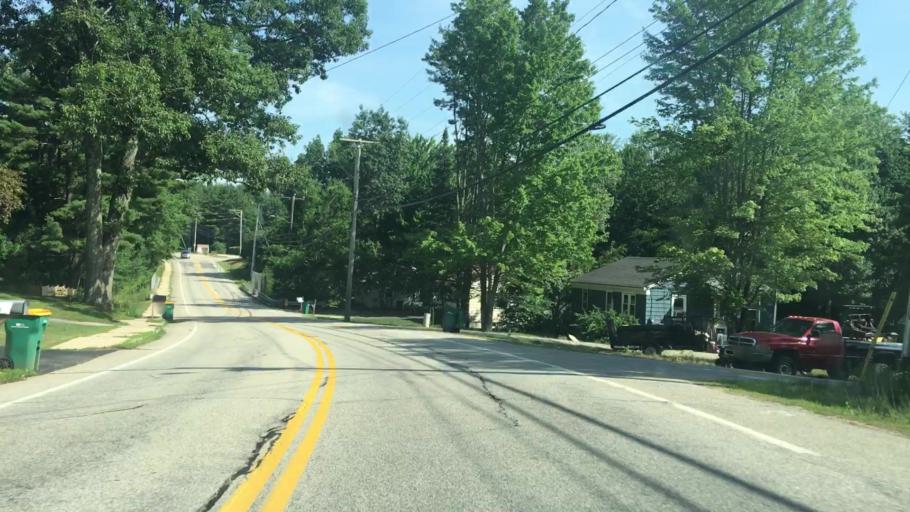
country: US
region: New Hampshire
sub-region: Strafford County
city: Rochester
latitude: 43.2835
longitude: -70.9746
